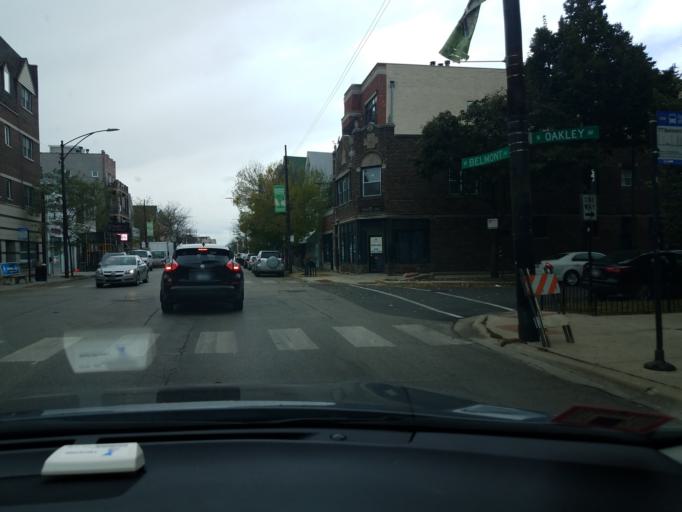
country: US
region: Illinois
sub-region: Cook County
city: Lincolnwood
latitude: 41.9395
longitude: -87.6853
